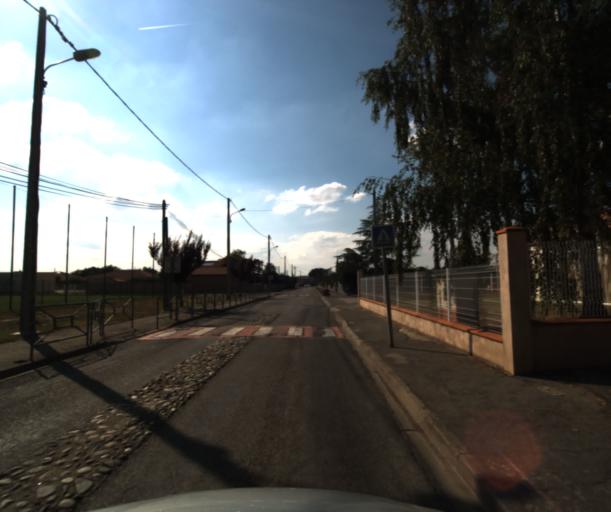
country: FR
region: Midi-Pyrenees
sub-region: Departement de la Haute-Garonne
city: Saint-Lys
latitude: 43.5107
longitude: 1.1829
